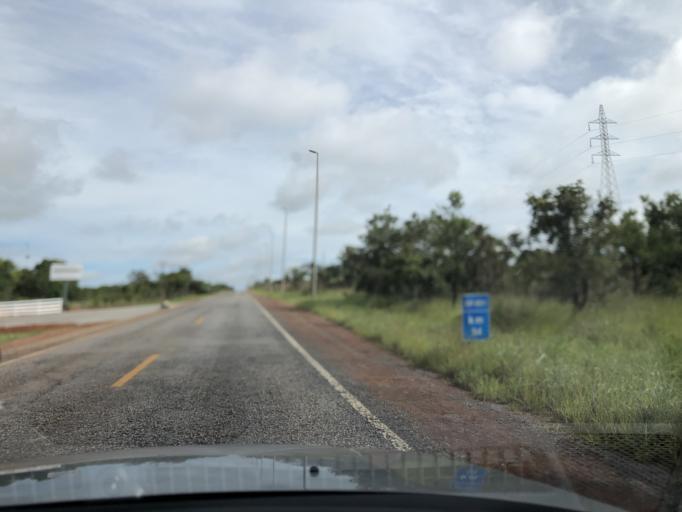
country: BR
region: Federal District
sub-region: Brasilia
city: Brasilia
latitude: -15.7063
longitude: -48.0878
